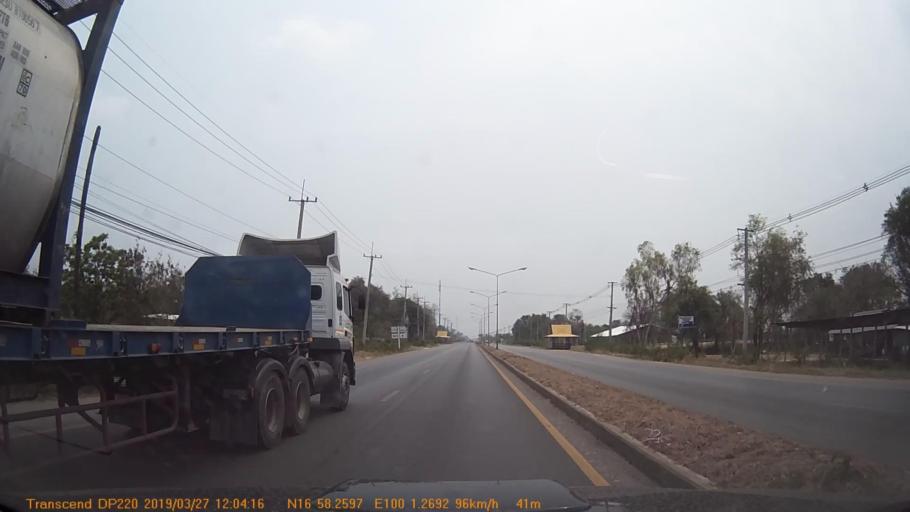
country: TH
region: Sukhothai
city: Kong Krailat
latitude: 16.9709
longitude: 100.0216
